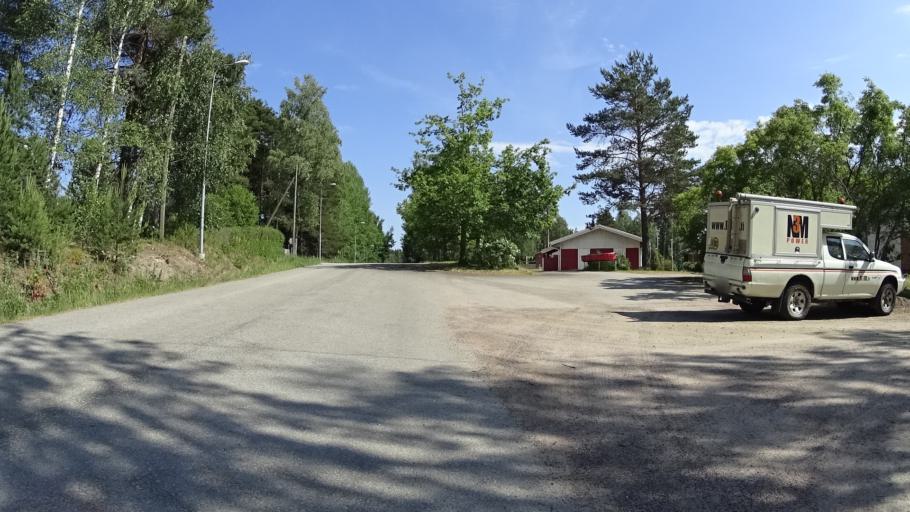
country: FI
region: Uusimaa
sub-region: Raaseporin
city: Karis
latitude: 60.0832
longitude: 23.6561
